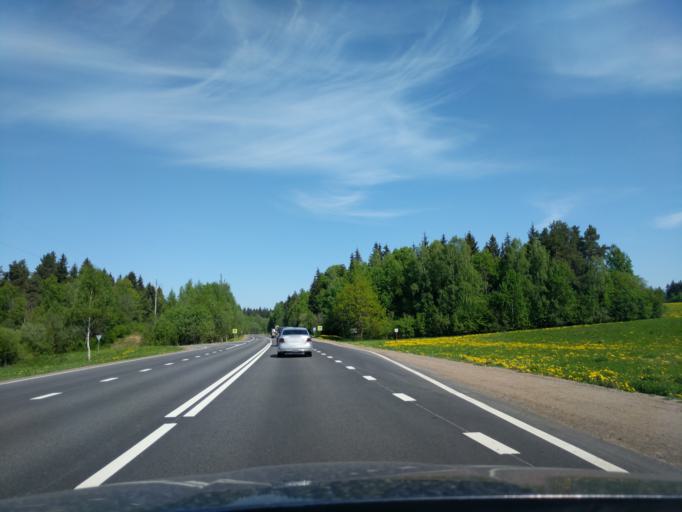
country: BY
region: Minsk
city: Bal'shavik
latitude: 54.1017
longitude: 27.5328
